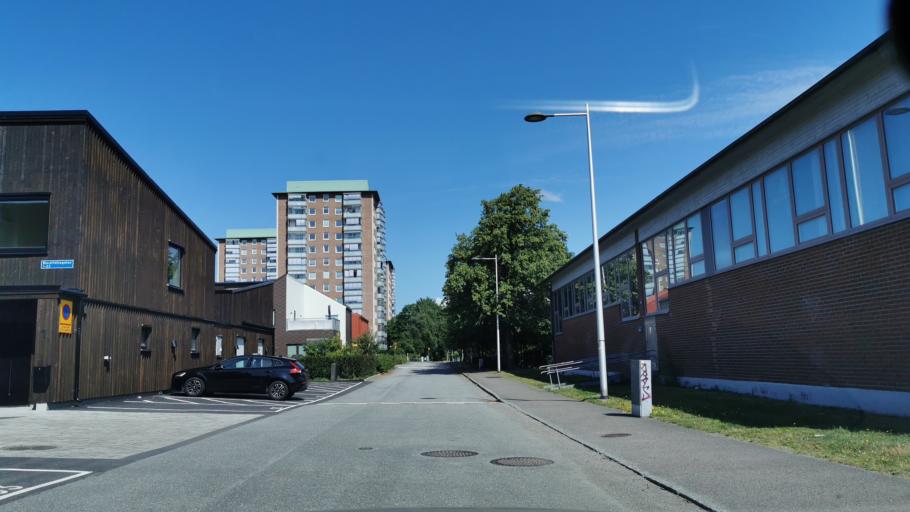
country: SE
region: Vaestra Goetaland
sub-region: Goteborg
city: Majorna
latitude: 57.6583
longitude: 11.9130
